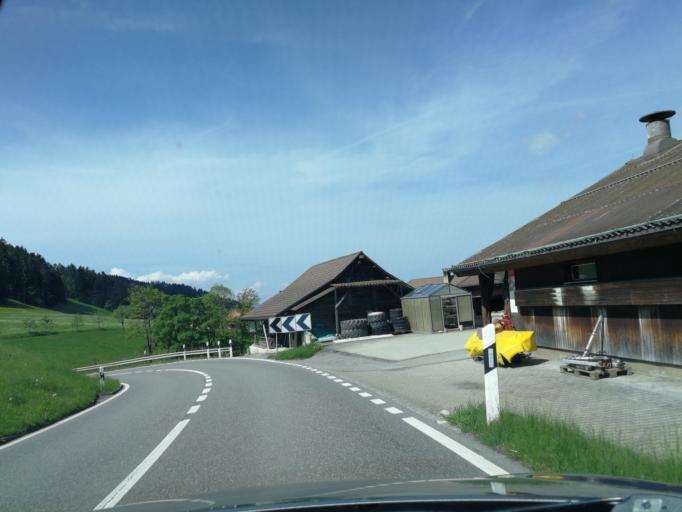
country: CH
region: Bern
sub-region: Bern-Mittelland District
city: Linden
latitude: 46.8387
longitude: 7.6593
